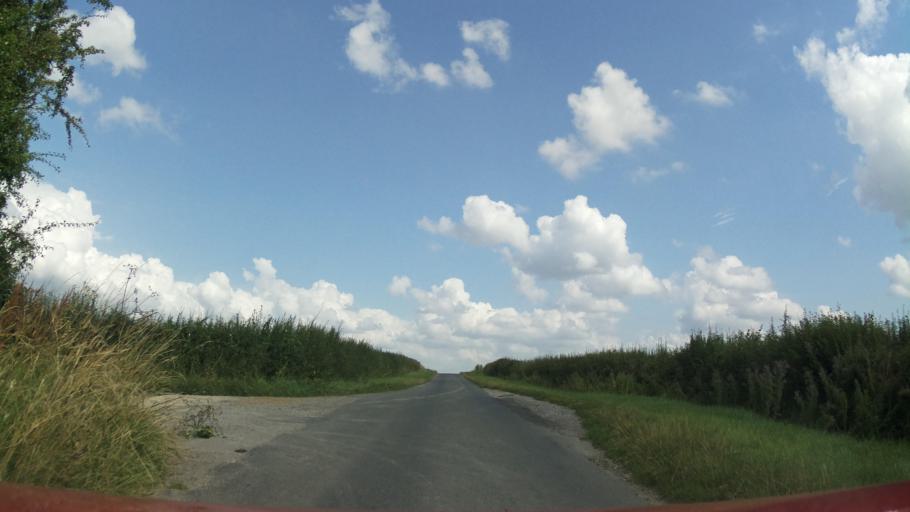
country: GB
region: England
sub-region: Wiltshire
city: Malmesbury
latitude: 51.5714
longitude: -2.1228
